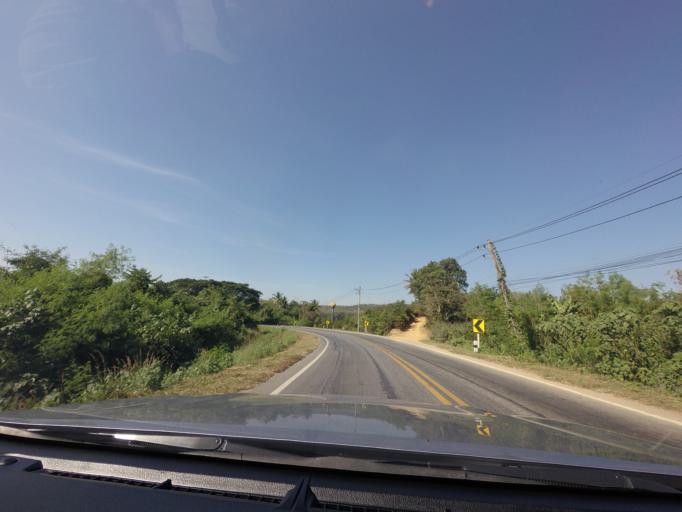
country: TH
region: Sukhothai
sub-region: Amphoe Si Satchanalai
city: Si Satchanalai
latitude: 17.6279
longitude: 99.7010
